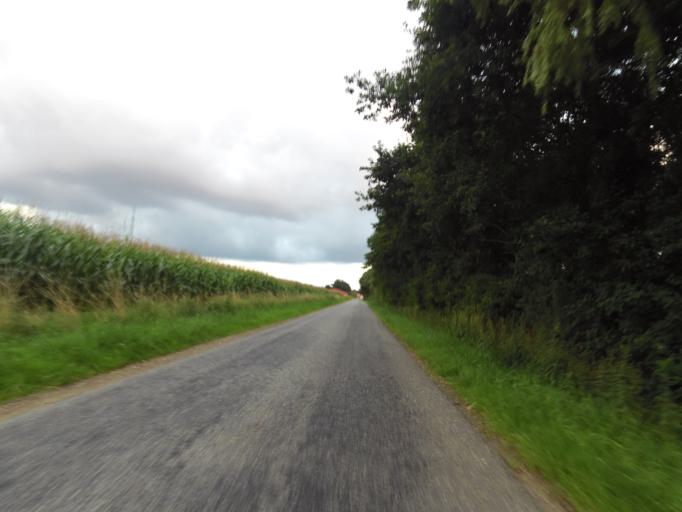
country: DK
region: South Denmark
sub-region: Esbjerg Kommune
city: Ribe
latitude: 55.2854
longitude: 8.8001
